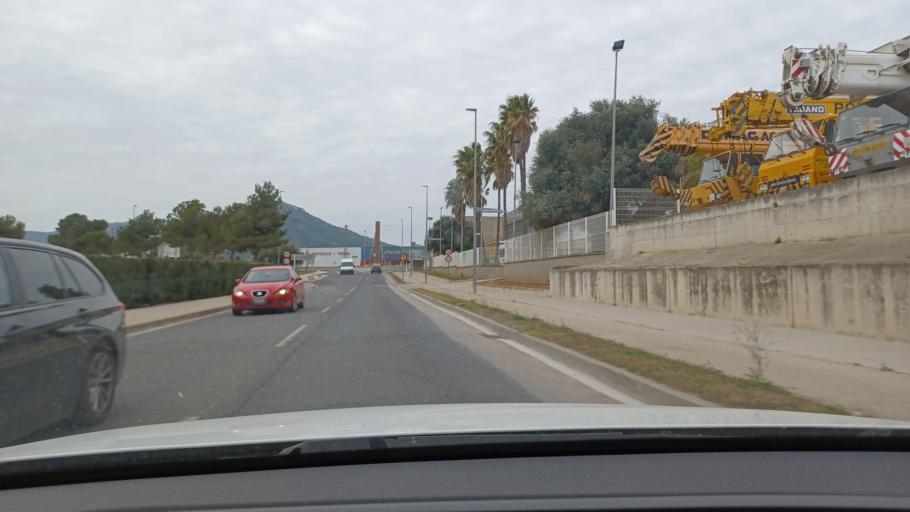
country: ES
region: Catalonia
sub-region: Provincia de Tarragona
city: Amposta
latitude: 40.7024
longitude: 0.5669
